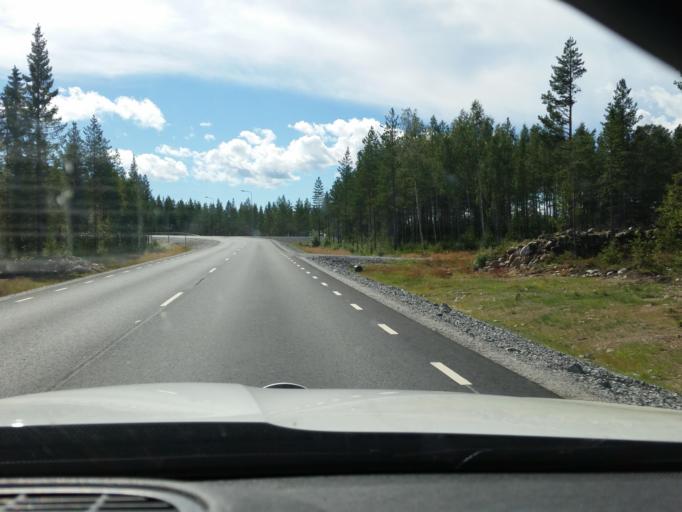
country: SE
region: Norrbotten
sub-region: Pitea Kommun
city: Norrfjarden
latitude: 65.3985
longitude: 21.4567
